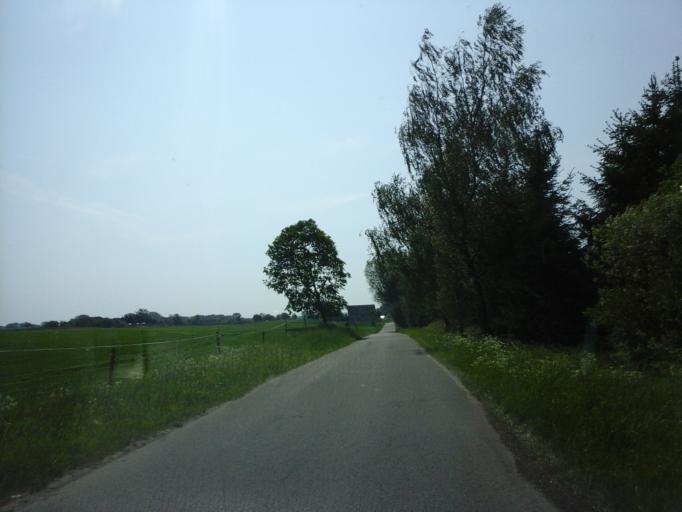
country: PL
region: West Pomeranian Voivodeship
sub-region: Powiat stargardzki
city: Insko
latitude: 53.3512
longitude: 15.5361
